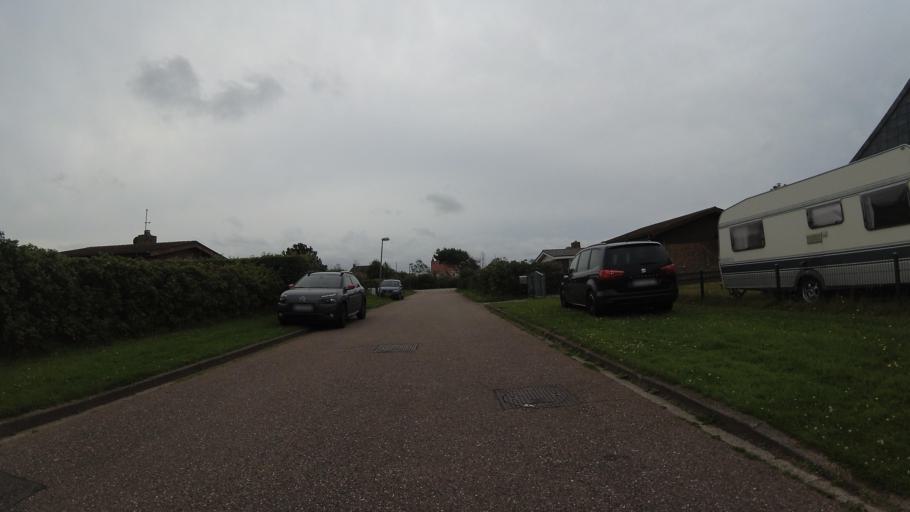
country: NL
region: North Holland
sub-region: Gemeente Den Helder
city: Den Helder
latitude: 52.9016
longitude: 4.7227
